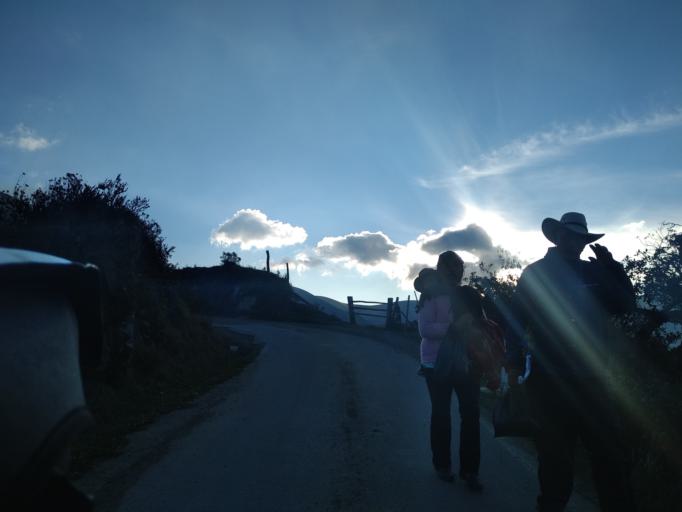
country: PE
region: Amazonas
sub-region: Provincia de Chachapoyas
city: Montevideo
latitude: -6.7098
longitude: -77.8694
